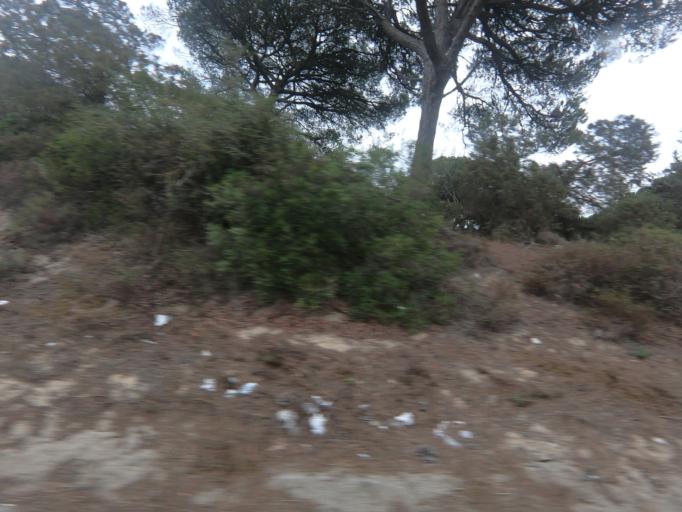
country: PT
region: Setubal
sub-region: Almada
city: Charneca
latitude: 38.5803
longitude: -9.1946
